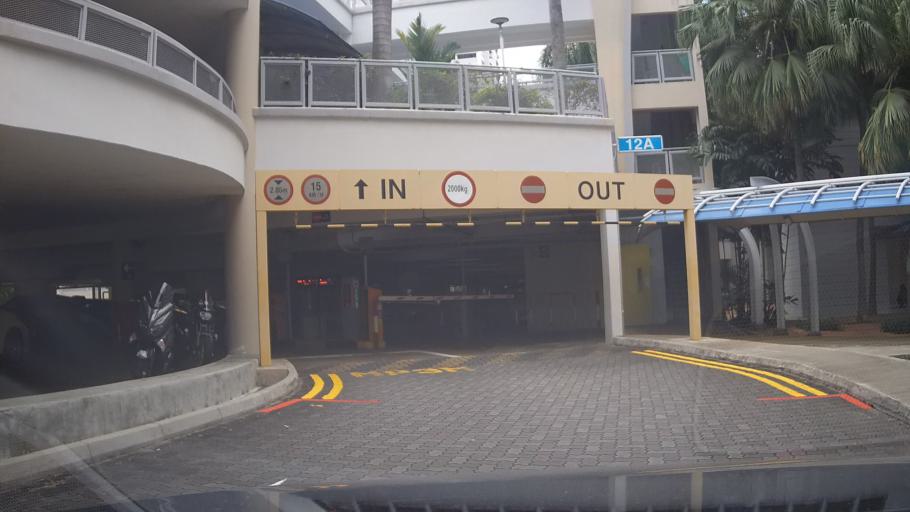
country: SG
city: Singapore
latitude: 1.3048
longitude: 103.9153
